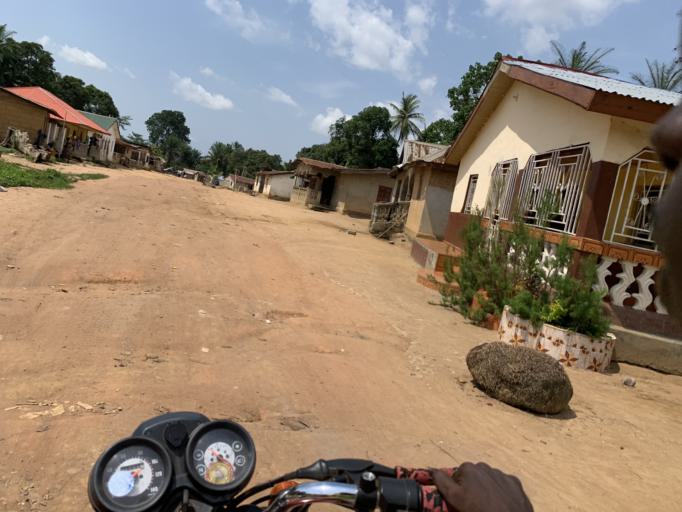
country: SL
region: Western Area
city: Waterloo
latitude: 8.3667
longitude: -13.0417
